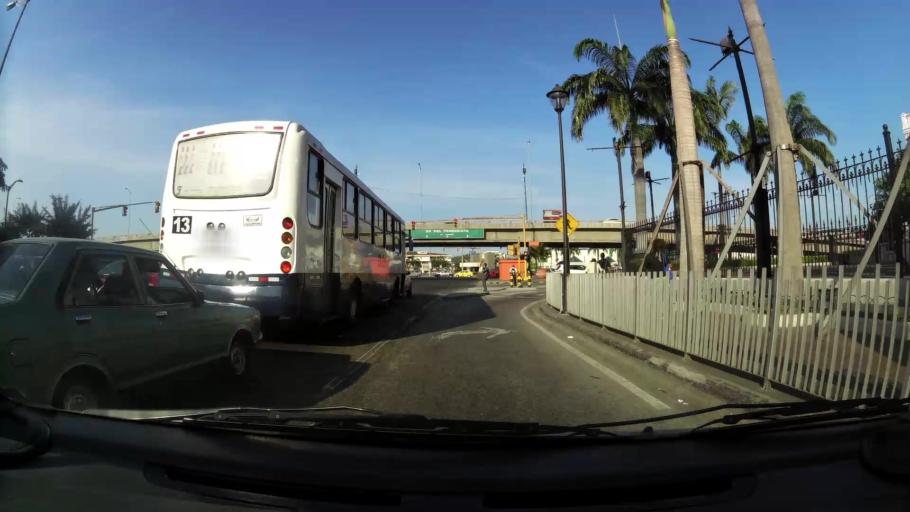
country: EC
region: Guayas
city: Guayaquil
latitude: -2.1702
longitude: -79.8983
